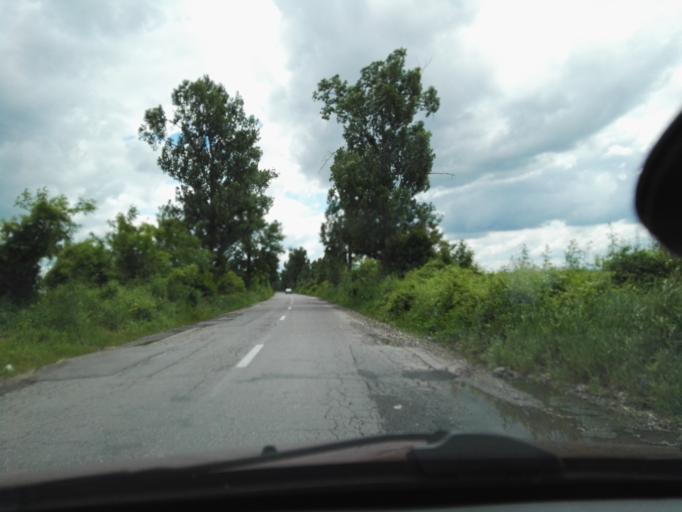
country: RO
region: Giurgiu
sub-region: Comuna Comana
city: Gradistea
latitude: 44.2307
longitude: 26.1306
